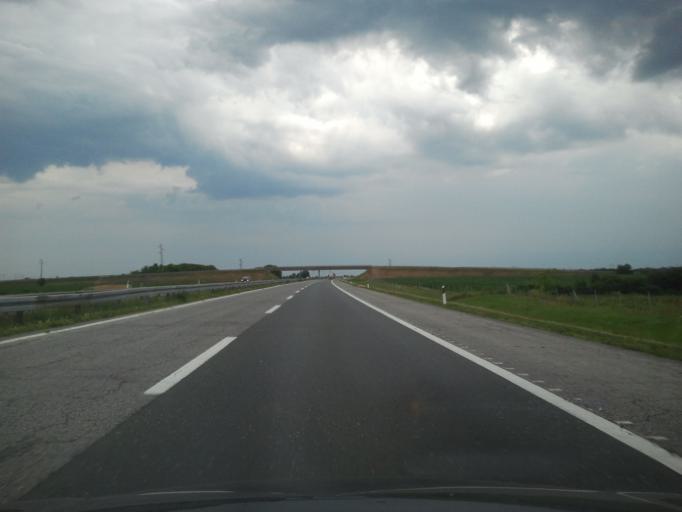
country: RS
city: Macvanska Mitrovica
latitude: 45.0144
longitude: 19.5722
